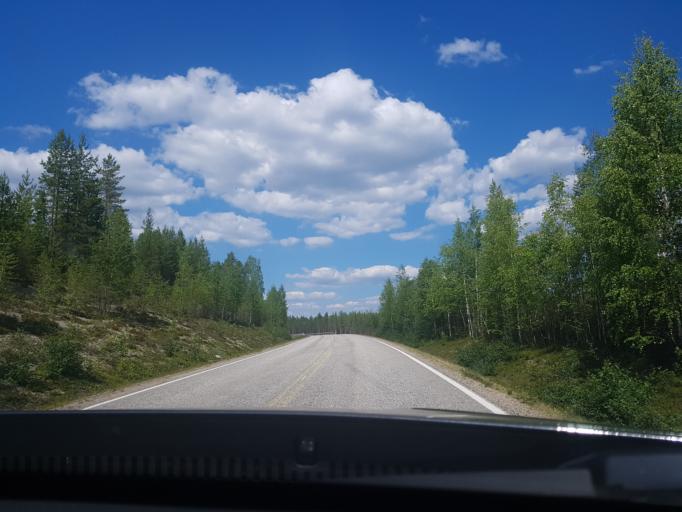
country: FI
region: Kainuu
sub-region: Kehys-Kainuu
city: Kuhmo
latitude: 64.2306
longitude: 29.8186
